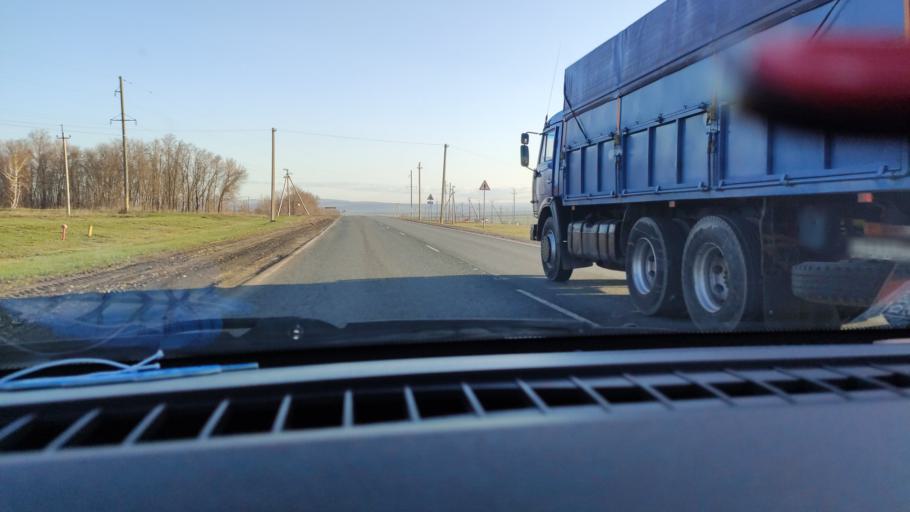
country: RU
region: Saratov
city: Balakovo
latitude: 52.1158
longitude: 47.7509
